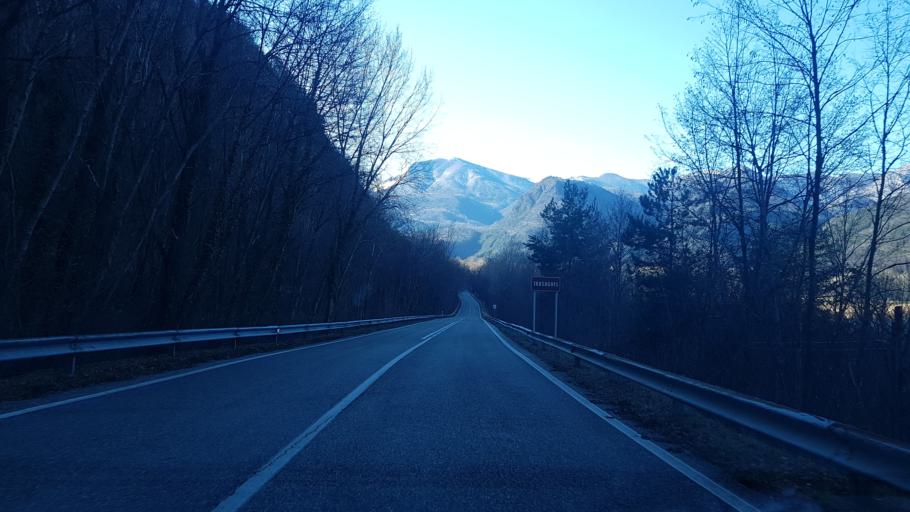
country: IT
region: Friuli Venezia Giulia
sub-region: Provincia di Udine
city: Bordano
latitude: 46.3237
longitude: 13.0757
